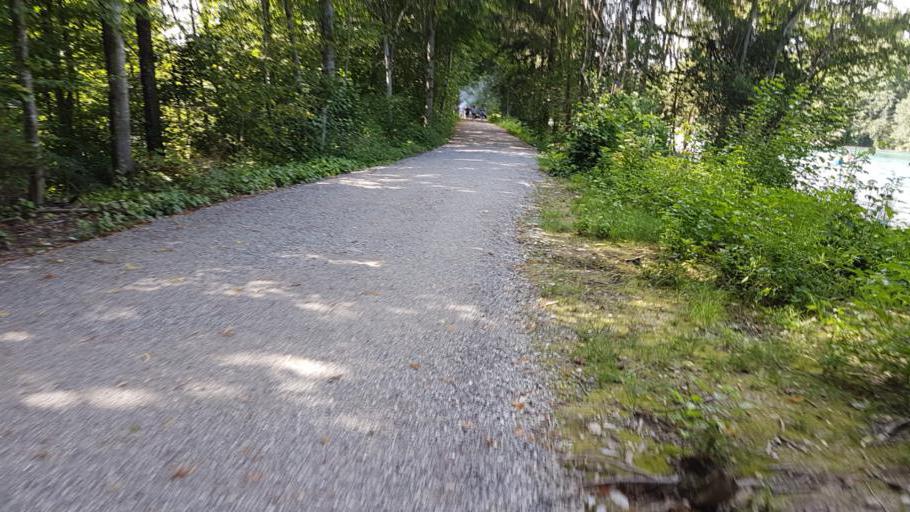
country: CH
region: Bern
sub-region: Bern-Mittelland District
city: Rubigen
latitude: 46.8944
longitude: 7.5326
